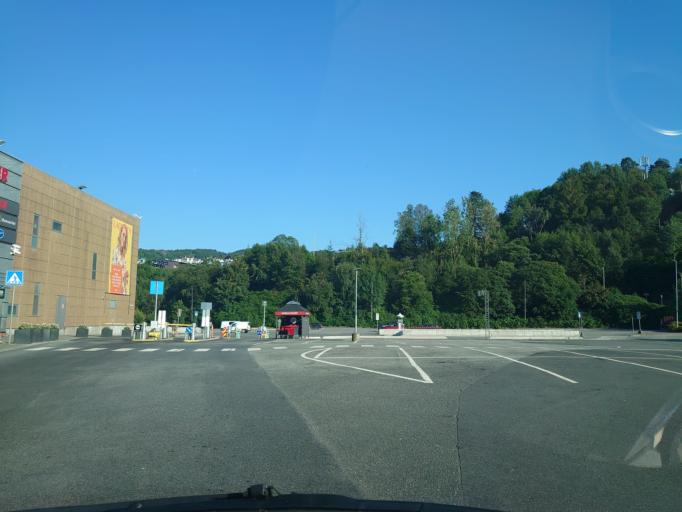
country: NO
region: Hordaland
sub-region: Bergen
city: Sandsli
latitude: 60.2962
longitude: 5.3298
